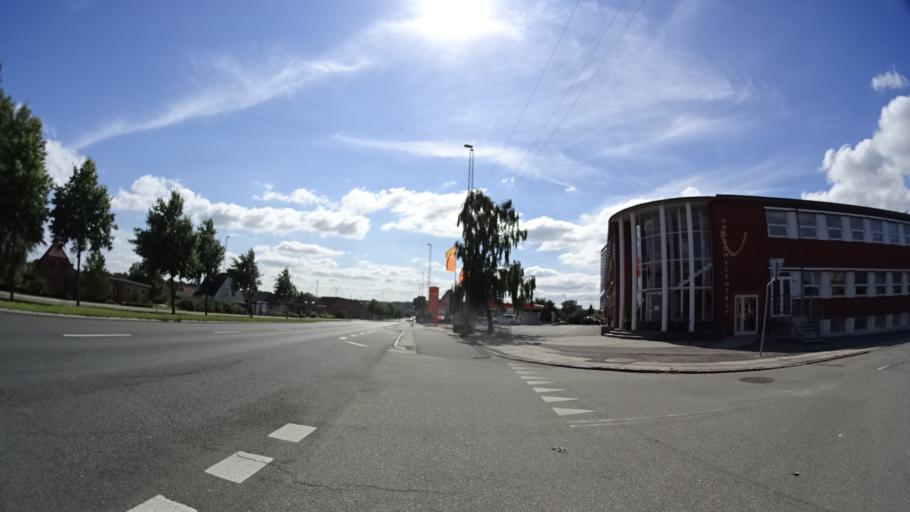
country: DK
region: Central Jutland
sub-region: Arhus Kommune
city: Arhus
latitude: 56.1330
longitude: 10.1690
